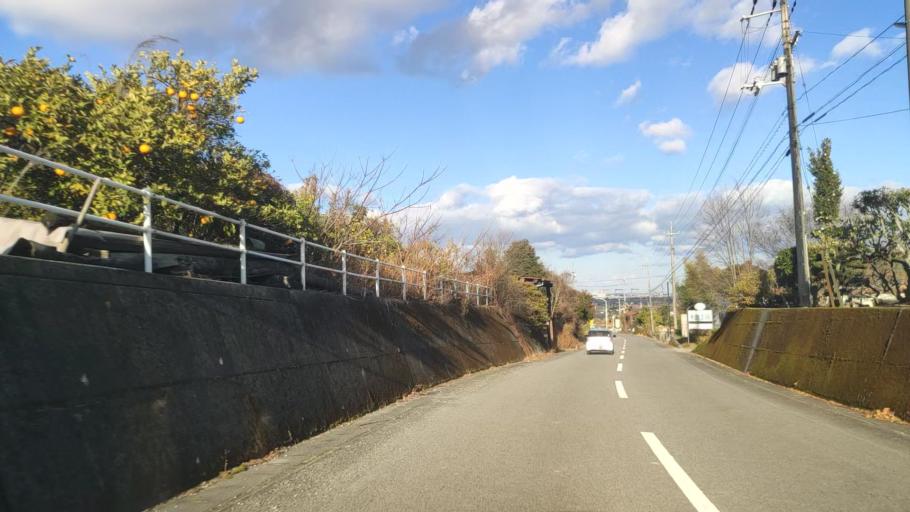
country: JP
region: Ehime
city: Saijo
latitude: 33.8884
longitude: 133.1295
